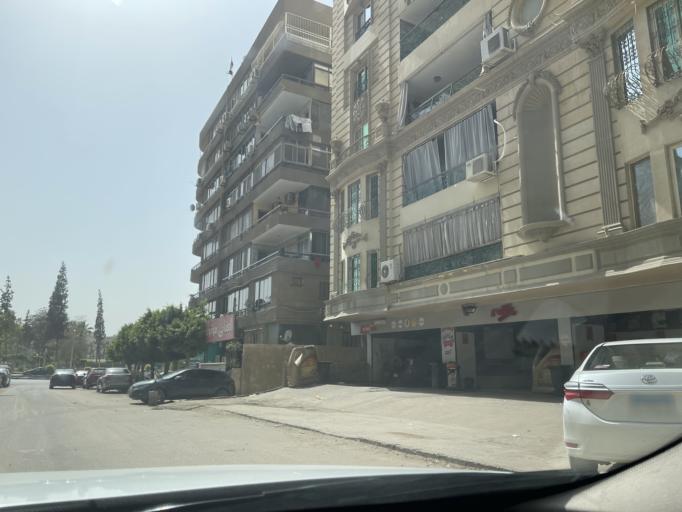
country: EG
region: Muhafazat al Qahirah
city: Cairo
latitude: 30.0618
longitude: 31.3506
